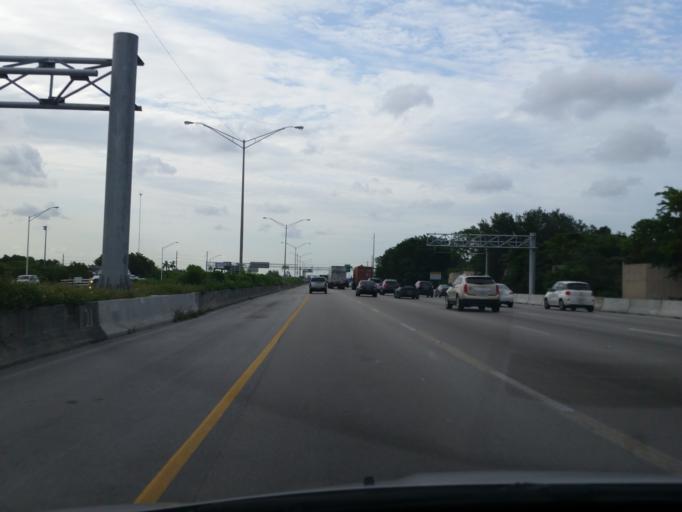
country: US
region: Florida
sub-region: Miami-Dade County
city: Ives Estates
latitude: 25.9693
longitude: -80.1654
